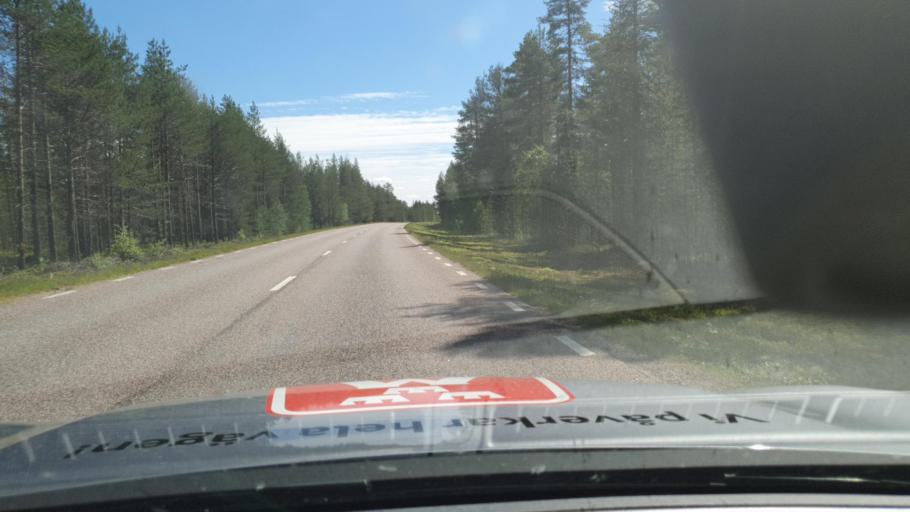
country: FI
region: Lapland
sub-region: Tunturi-Lappi
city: Kolari
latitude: 67.0232
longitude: 23.7248
